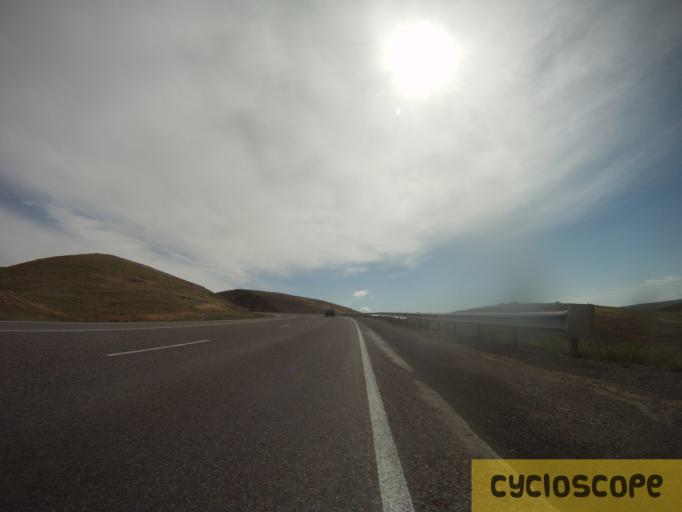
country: KZ
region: Zhambyl
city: Georgiyevka
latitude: 43.2615
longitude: 74.8329
